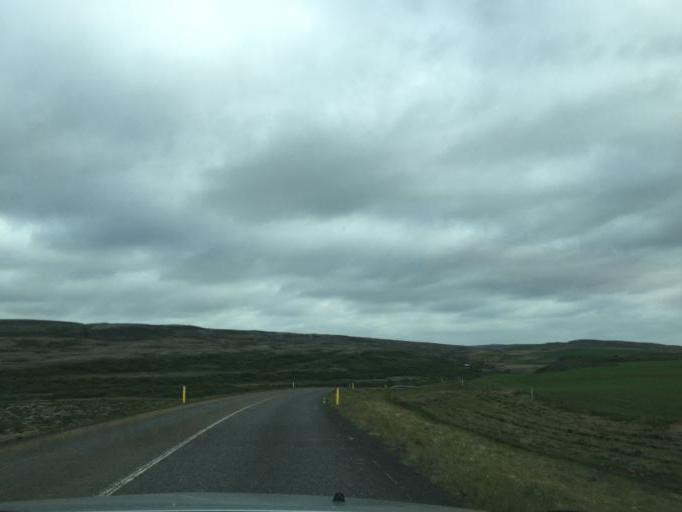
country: IS
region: South
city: Vestmannaeyjar
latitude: 64.2663
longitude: -20.2238
